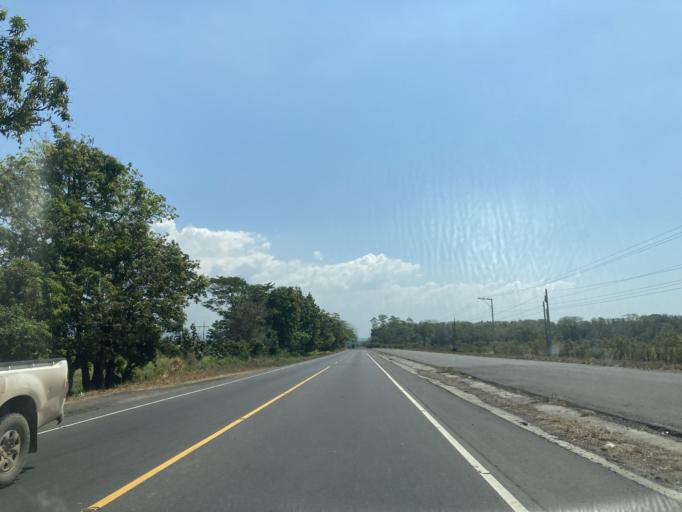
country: GT
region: Escuintla
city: Guanagazapa
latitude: 14.1066
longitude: -90.6282
